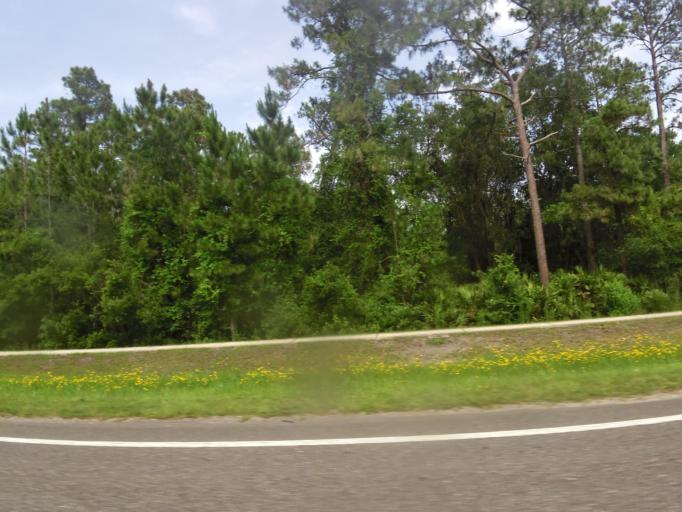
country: US
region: Florida
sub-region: Saint Johns County
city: Saint Augustine
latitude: 29.9054
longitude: -81.3610
